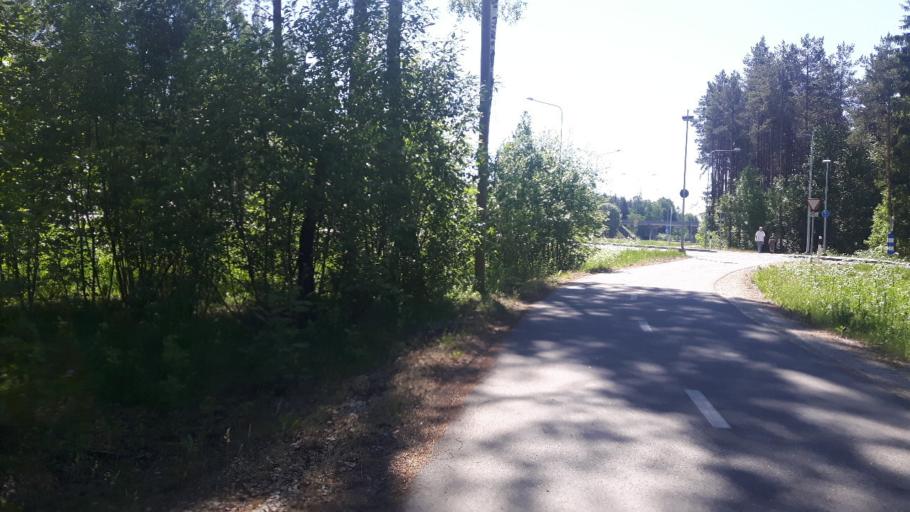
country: EE
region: Harju
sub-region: Saku vald
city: Saku
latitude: 59.3168
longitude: 24.6855
